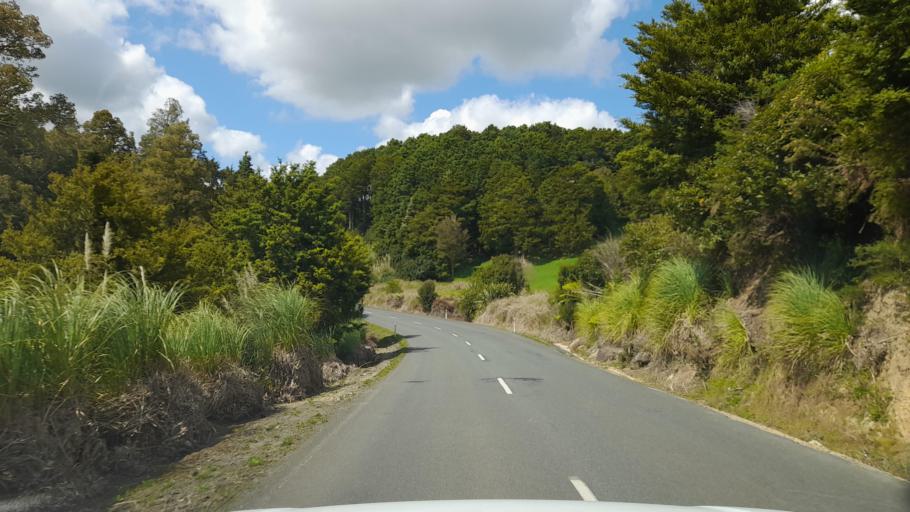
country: NZ
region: Northland
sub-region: Whangarei
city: Maungatapere
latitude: -35.6352
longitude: 174.0727
